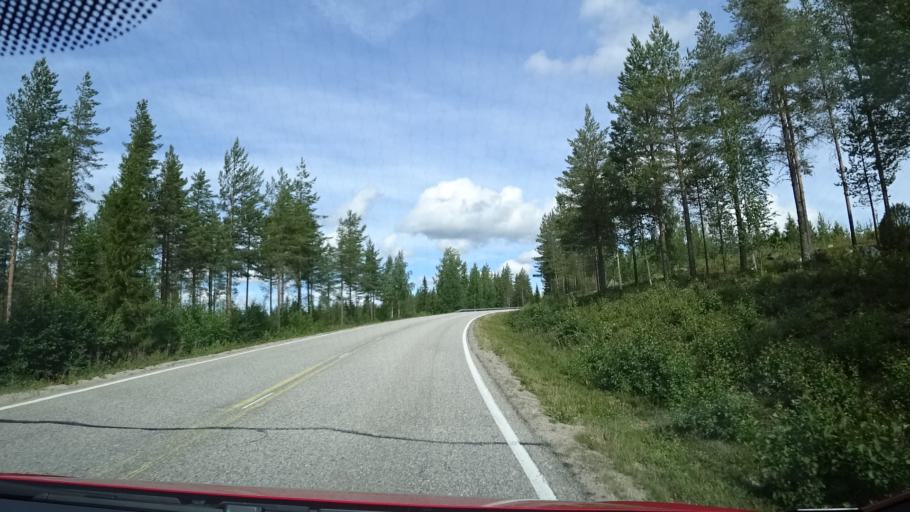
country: FI
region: Kainuu
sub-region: Kehys-Kainuu
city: Kuhmo
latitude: 64.4342
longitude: 29.8088
